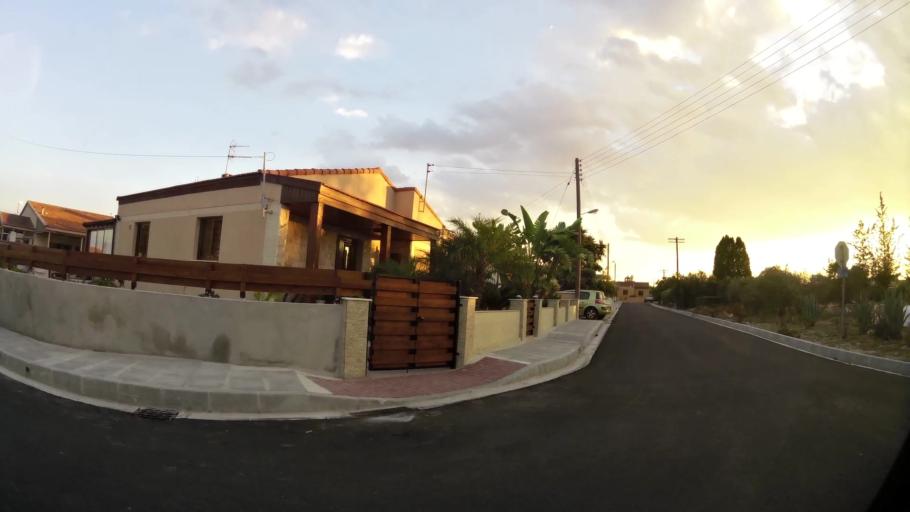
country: CY
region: Larnaka
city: Dhromolaxia
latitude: 34.8697
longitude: 33.5870
